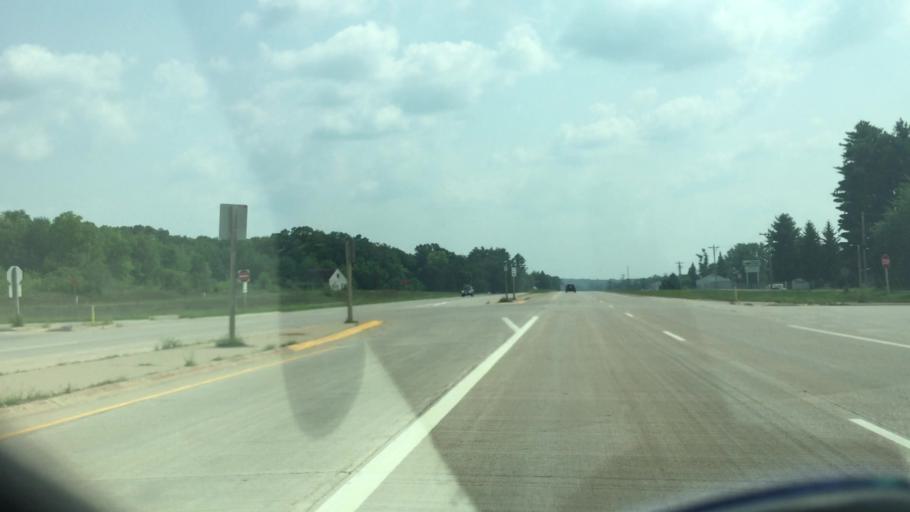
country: US
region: Wisconsin
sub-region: Eau Claire County
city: Altoona
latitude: 44.7525
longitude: -91.4543
